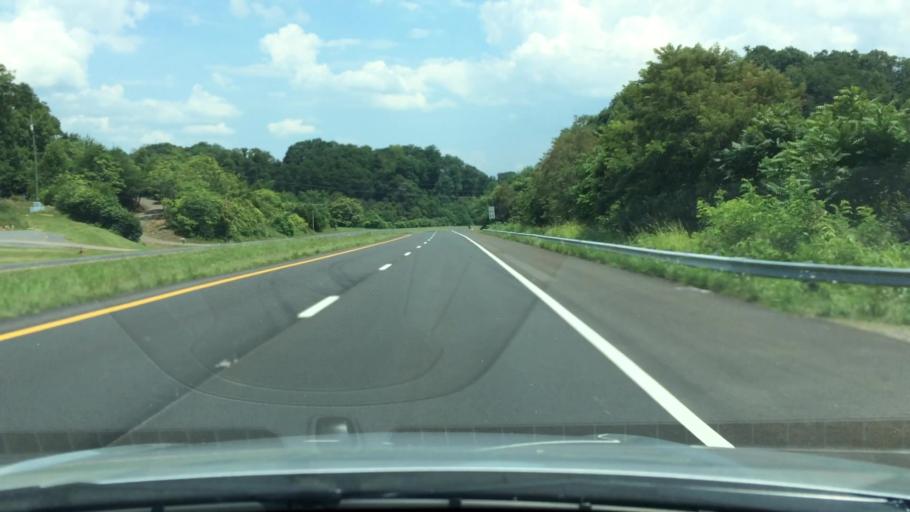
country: US
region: Tennessee
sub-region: Hamblen County
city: Morristown
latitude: 36.1894
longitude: -83.2634
